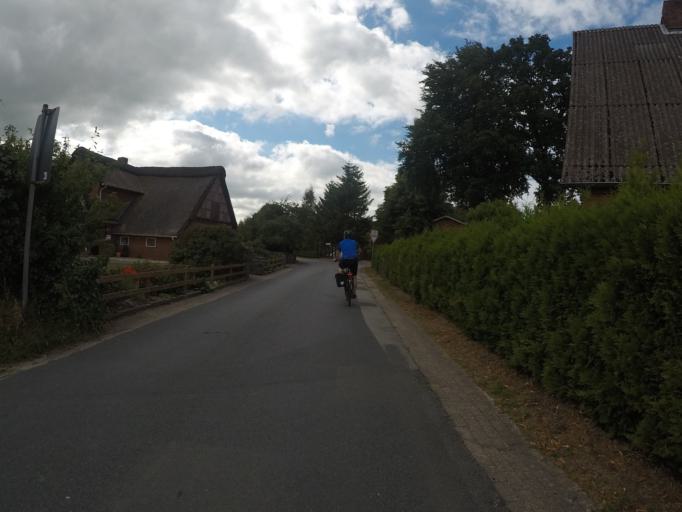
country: DE
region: Lower Saxony
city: Cadenberge
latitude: 53.7556
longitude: 9.0403
